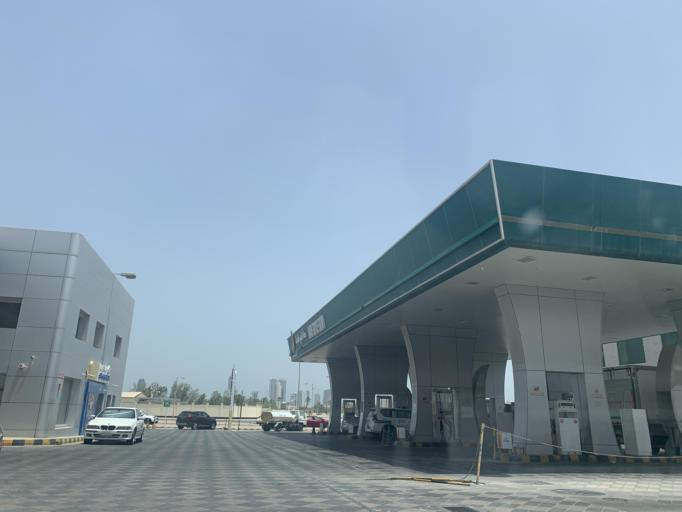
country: BH
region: Manama
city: Jidd Hafs
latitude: 26.2073
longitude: 50.5514
